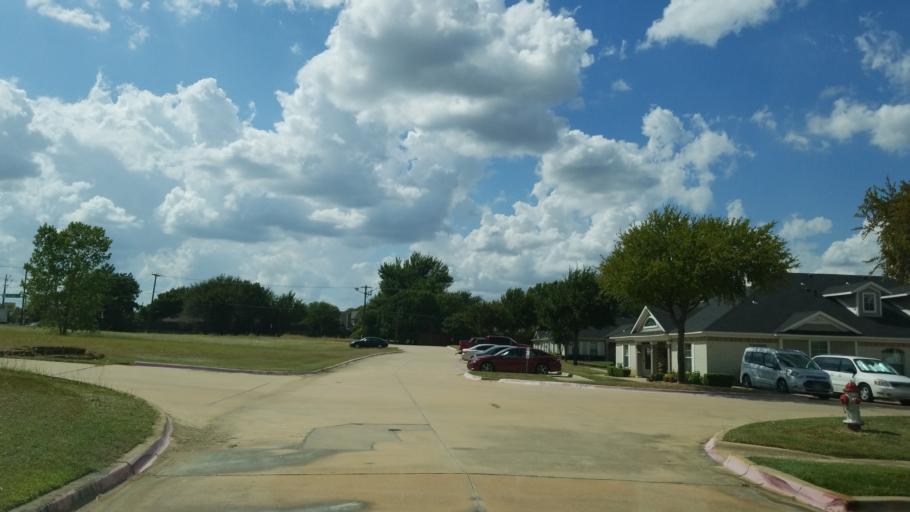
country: US
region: Texas
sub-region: Tarrant County
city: Euless
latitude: 32.8819
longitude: -97.0809
